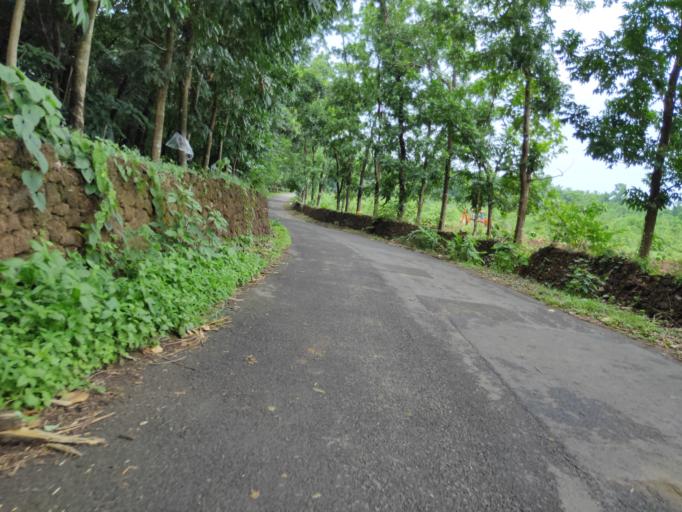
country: IN
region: Kerala
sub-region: Malappuram
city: Manjeri
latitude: 11.2319
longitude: 76.2498
